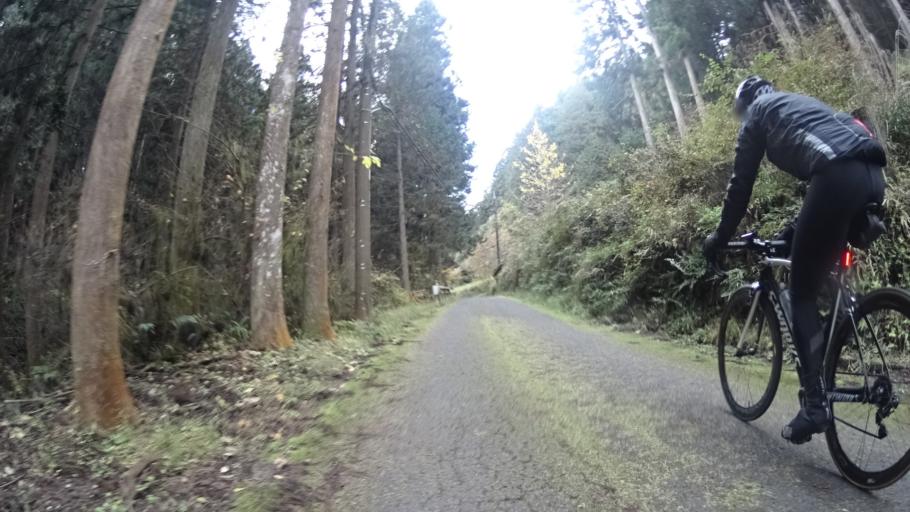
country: JP
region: Saitama
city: Morohongo
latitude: 35.9094
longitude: 139.2098
